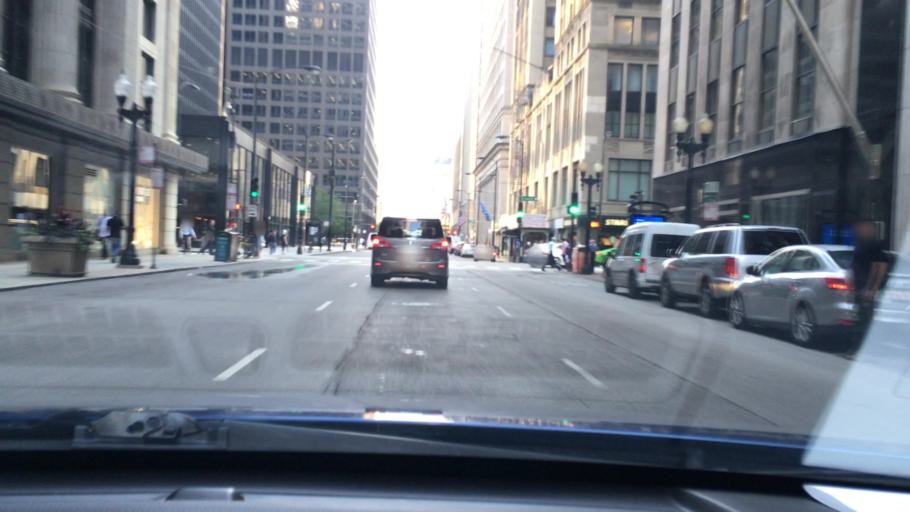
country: US
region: Illinois
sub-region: Cook County
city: Chicago
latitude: 41.8801
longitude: -87.6308
